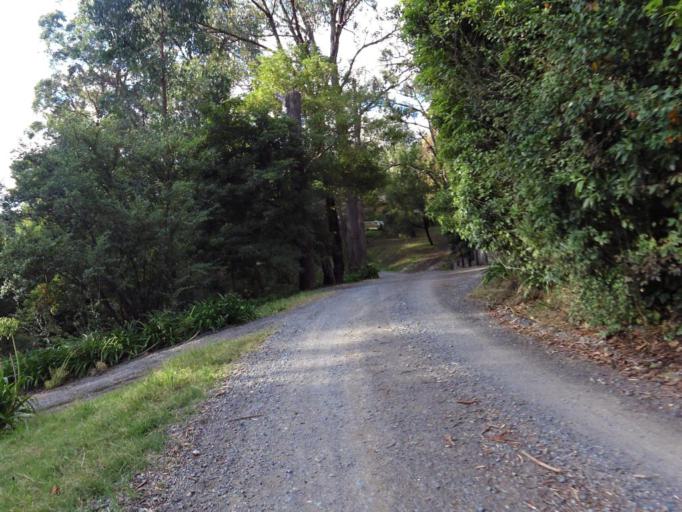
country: AU
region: Victoria
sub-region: Yarra Ranges
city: Mount Evelyn
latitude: -37.7934
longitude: 145.3854
